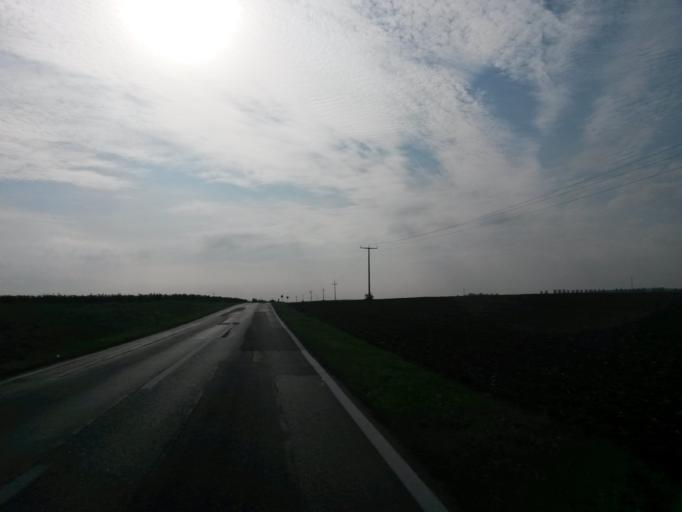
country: HR
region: Vukovarsko-Srijemska
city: Lovas
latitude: 45.2795
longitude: 19.1304
